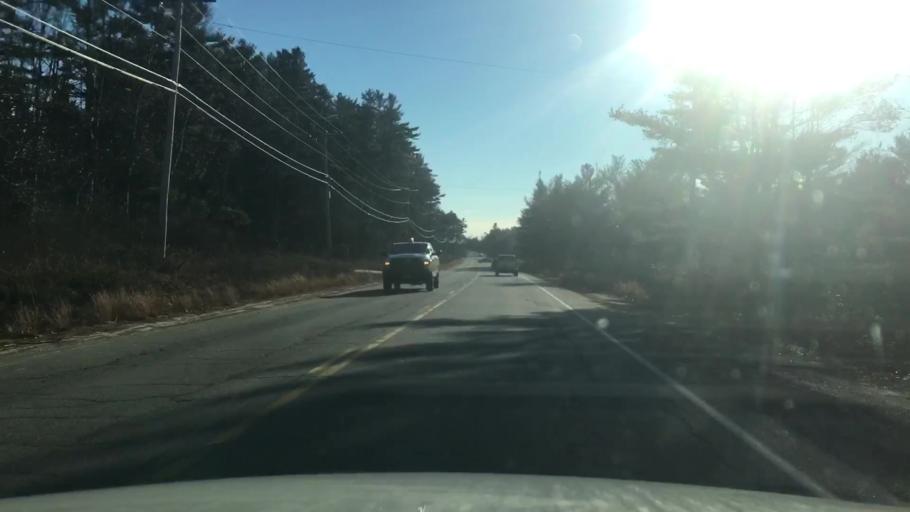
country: US
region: Maine
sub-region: Cumberland County
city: Brunswick
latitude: 43.8756
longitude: -69.9123
